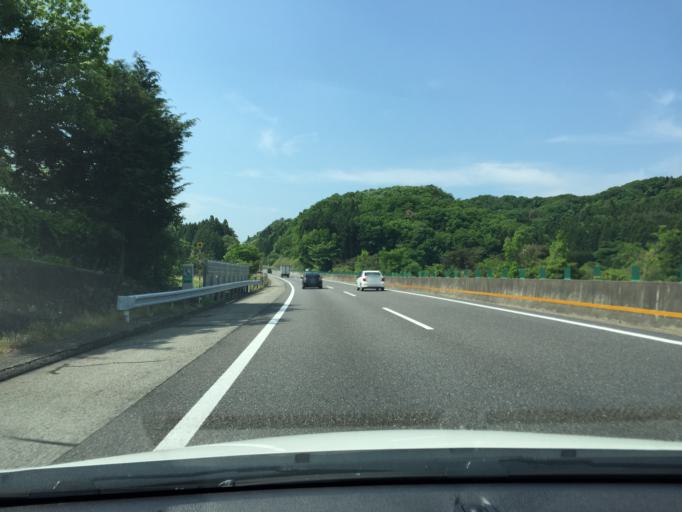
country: JP
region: Fukushima
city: Sukagawa
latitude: 37.1755
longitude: 140.2723
